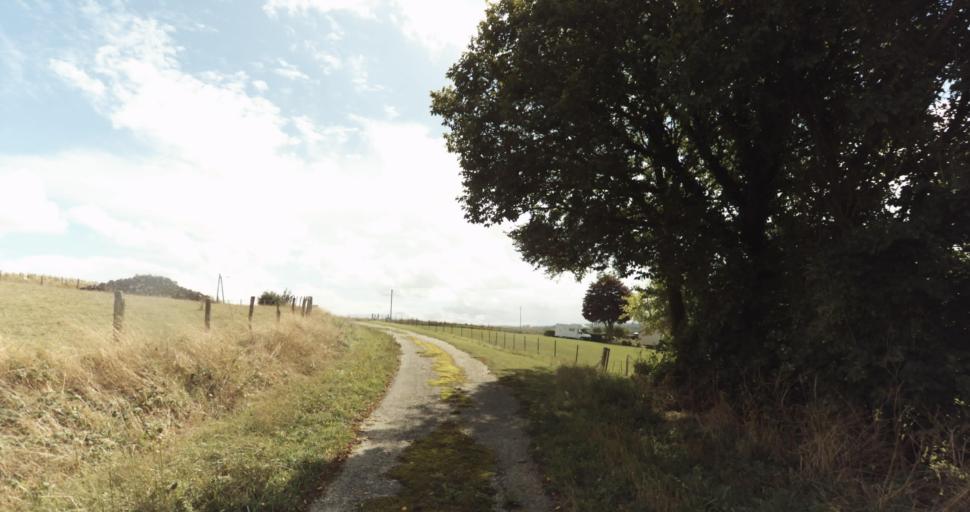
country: FR
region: Lower Normandy
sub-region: Departement de l'Orne
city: Gace
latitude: 48.7755
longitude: 0.3121
